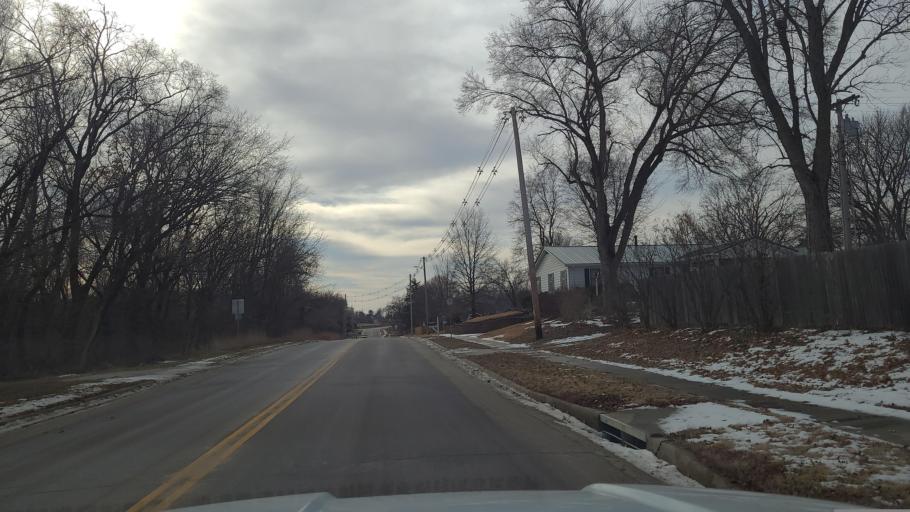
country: US
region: Kansas
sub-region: Douglas County
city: Baldwin City
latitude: 38.7716
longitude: -95.1861
